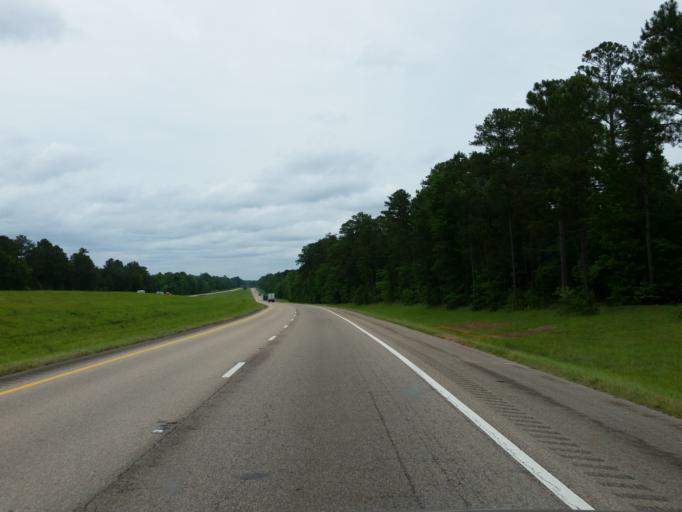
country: US
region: Mississippi
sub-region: Clarke County
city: Stonewall
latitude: 32.0196
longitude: -88.9231
